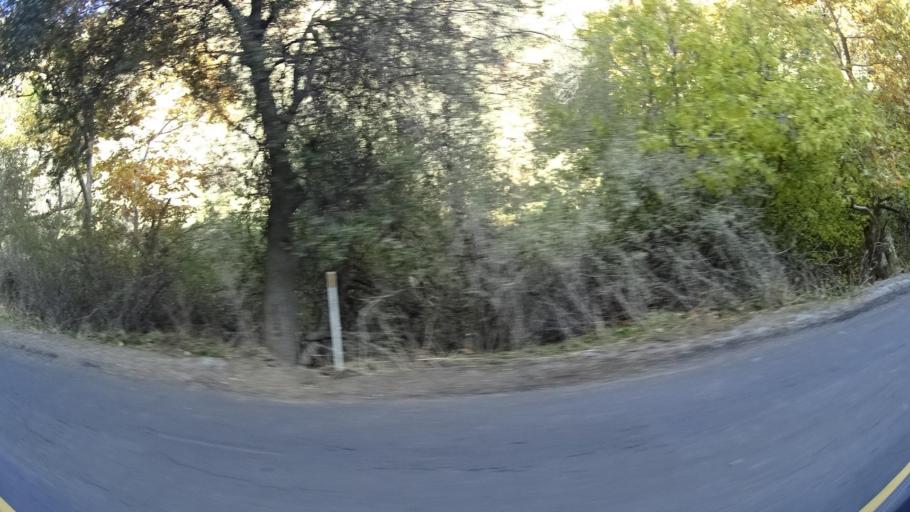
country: US
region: California
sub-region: Kern County
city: Bear Valley Springs
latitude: 35.3205
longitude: -118.5895
